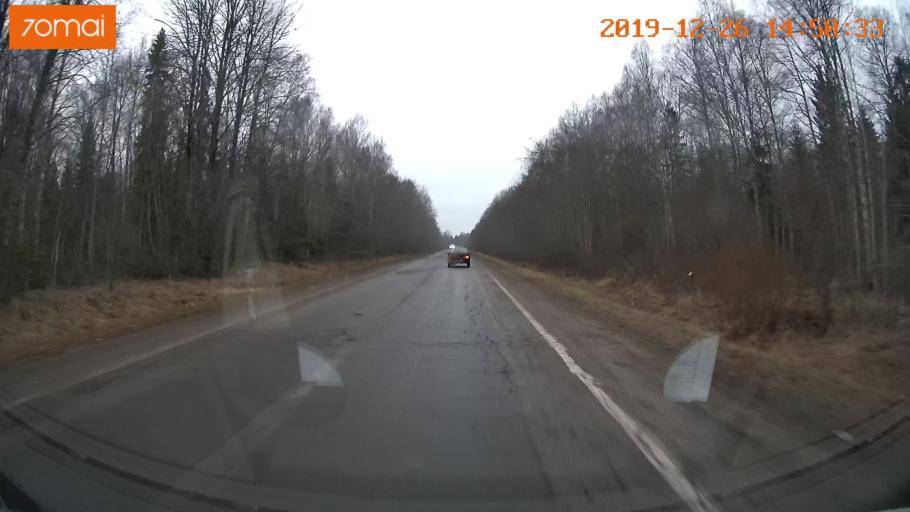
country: RU
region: Jaroslavl
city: Poshekhon'ye
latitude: 58.3310
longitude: 38.9235
